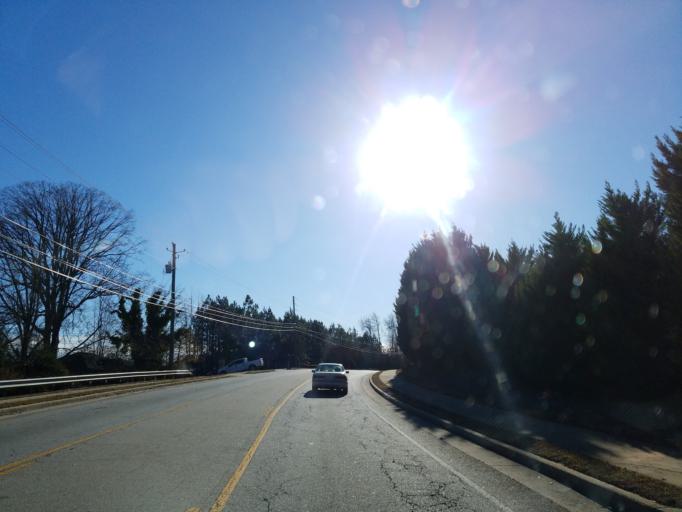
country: US
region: Georgia
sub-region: Cobb County
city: Mableton
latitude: 33.8044
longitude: -84.5108
